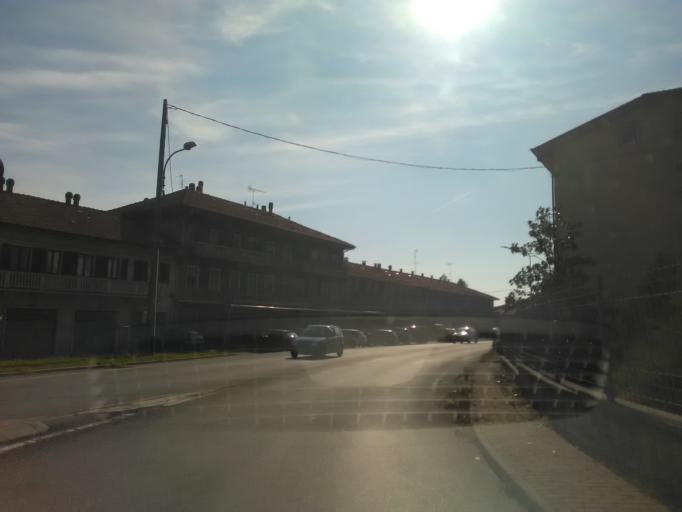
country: IT
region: Piedmont
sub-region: Provincia di Novara
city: Prato Sesia
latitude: 45.6359
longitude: 8.3721
